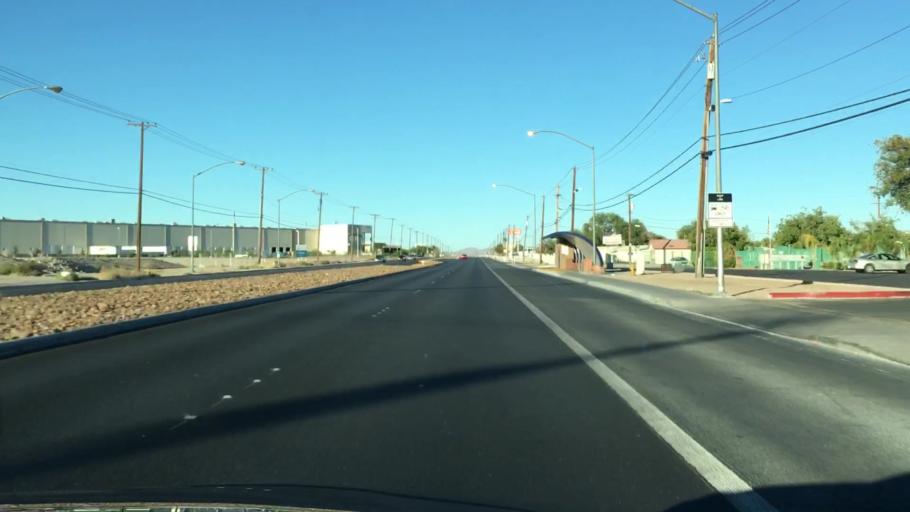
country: US
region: Nevada
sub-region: Clark County
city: Sunrise Manor
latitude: 36.2204
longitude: -115.0886
